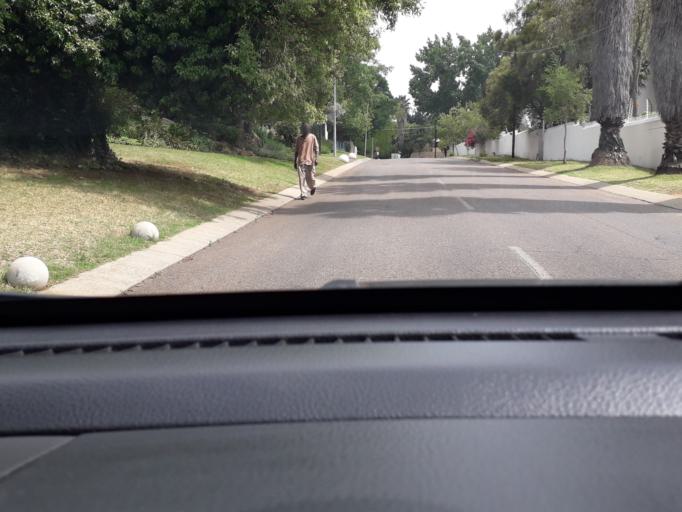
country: ZA
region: Gauteng
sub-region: City of Johannesburg Metropolitan Municipality
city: Modderfontein
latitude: -26.0945
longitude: 28.0717
